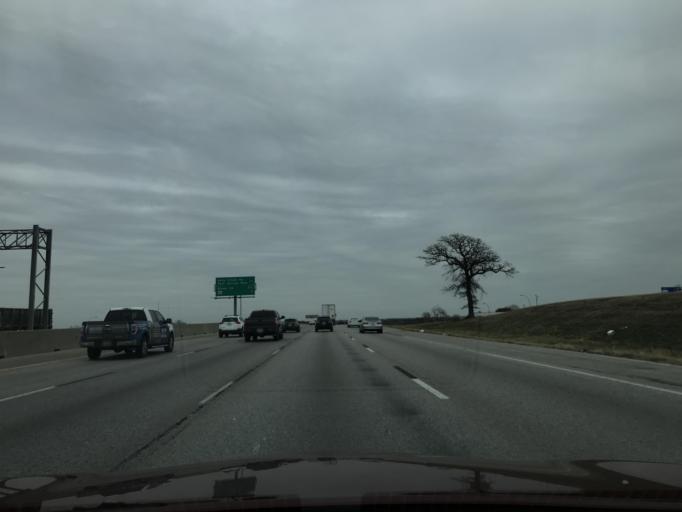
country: US
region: Texas
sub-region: Tarrant County
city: Kennedale
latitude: 32.6743
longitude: -97.1954
